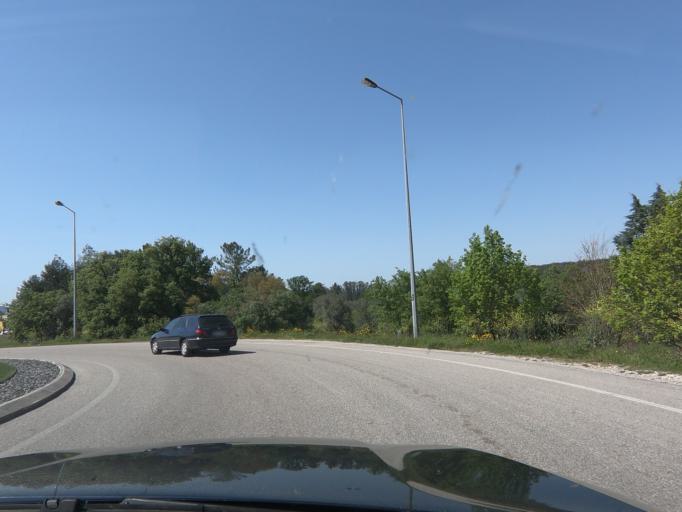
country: PT
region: Coimbra
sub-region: Lousa
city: Lousa
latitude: 40.1291
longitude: -8.2481
